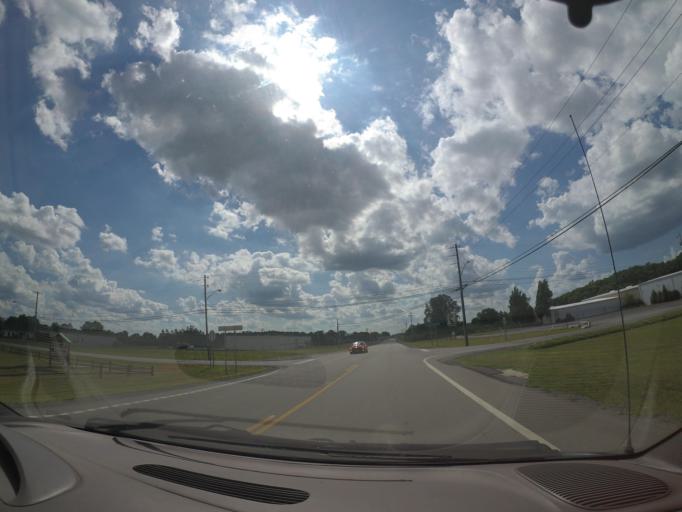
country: US
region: Ohio
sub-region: Huron County
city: Norwalk
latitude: 41.2496
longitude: -82.5662
